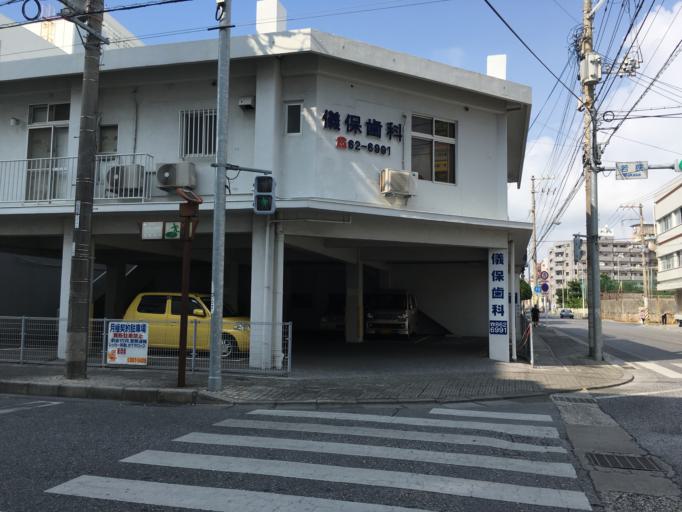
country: JP
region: Okinawa
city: Naha-shi
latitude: 26.2211
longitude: 127.6777
